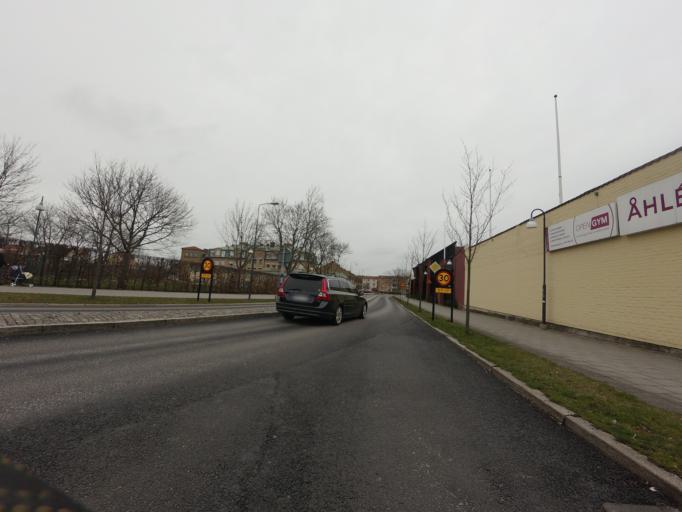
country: SE
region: Skane
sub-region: Ystads Kommun
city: Ystad
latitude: 55.4325
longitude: 13.8184
